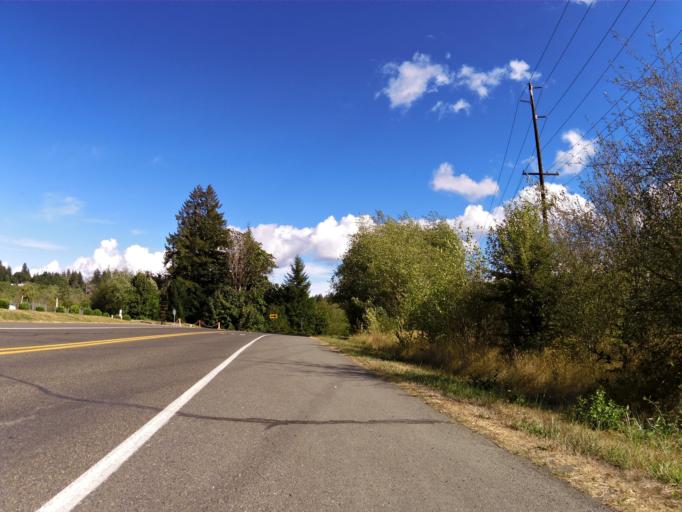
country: US
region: Washington
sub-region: Thurston County
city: Olympia
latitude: 47.0477
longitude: -122.9932
